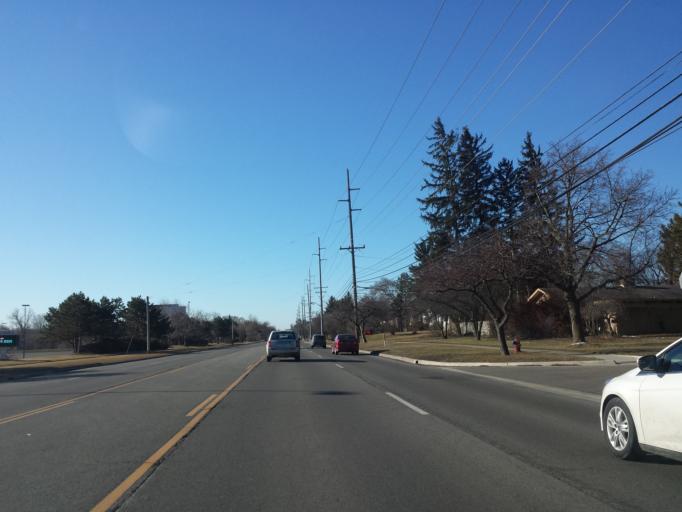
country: US
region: Michigan
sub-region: Oakland County
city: Troy
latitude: 42.5726
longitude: -83.1482
